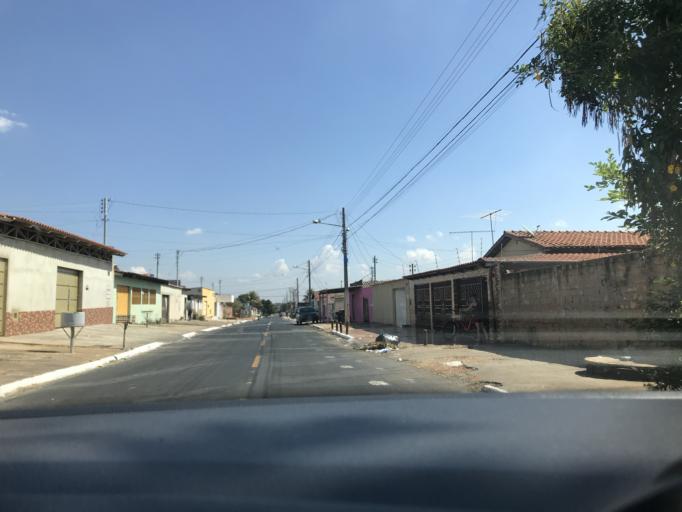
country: BR
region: Goias
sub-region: Senador Canedo
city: Senador Canedo
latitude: -16.6511
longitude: -49.1579
